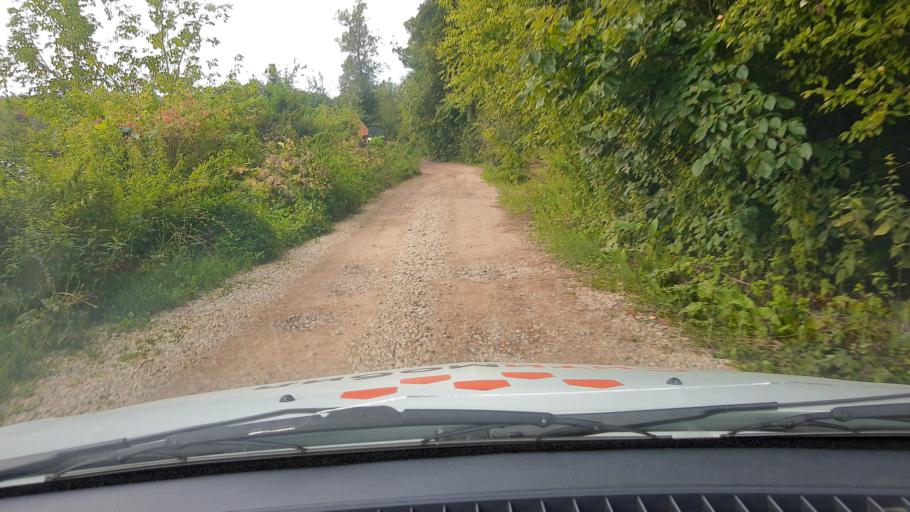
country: RU
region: Bashkortostan
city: Kabakovo
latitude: 54.7102
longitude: 56.1391
